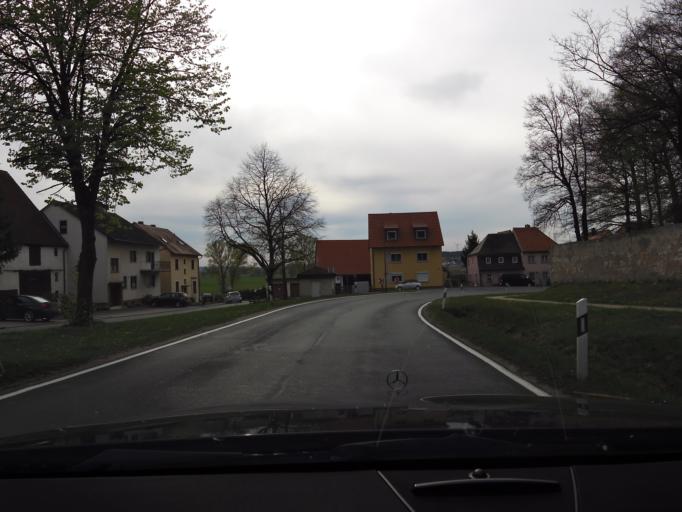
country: DE
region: Bavaria
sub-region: Upper Franconia
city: Pommersfelden
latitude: 49.7624
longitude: 10.8174
